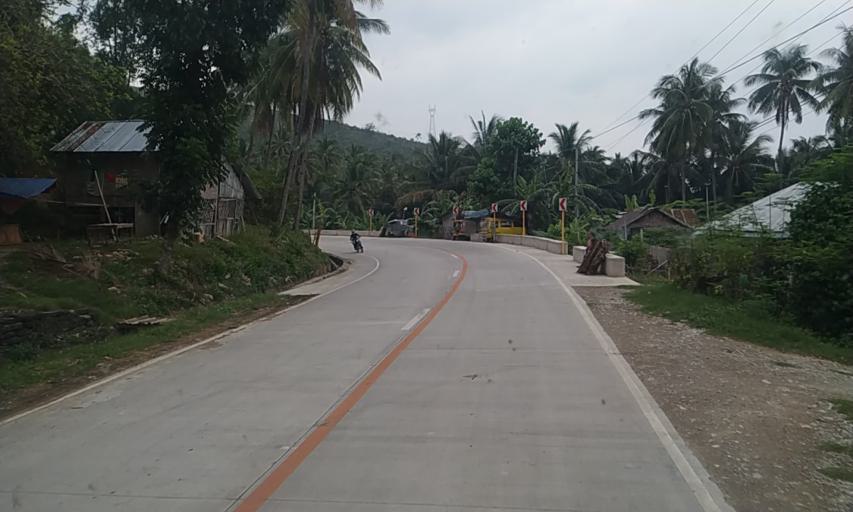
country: PH
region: Central Visayas
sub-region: Province of Negros Oriental
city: Calamba
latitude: 10.1940
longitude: 123.2953
